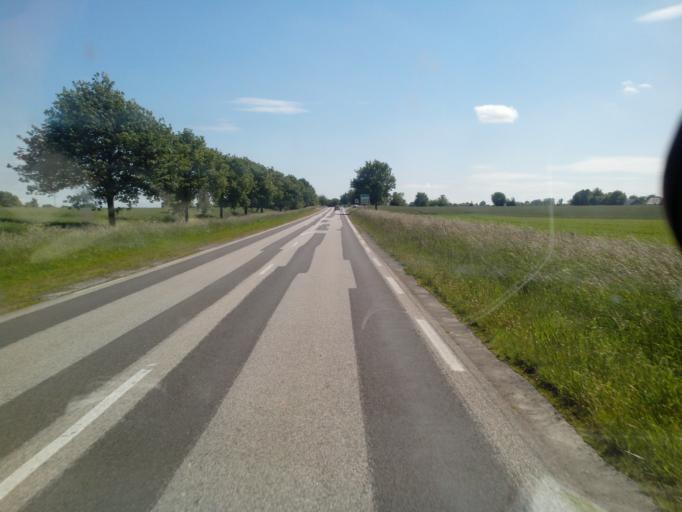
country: FR
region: Haute-Normandie
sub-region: Departement de l'Eure
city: Beuzeville
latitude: 49.3715
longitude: 0.3971
